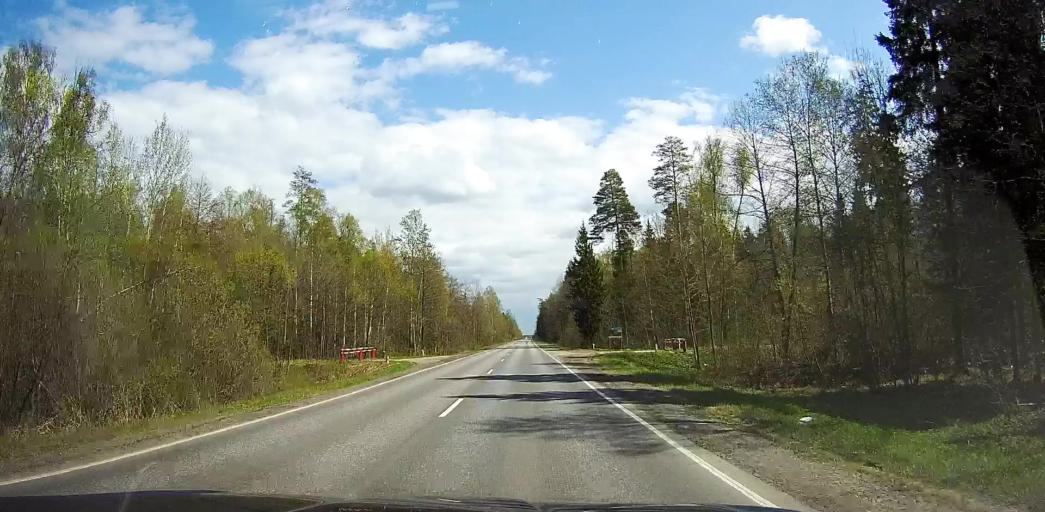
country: RU
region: Moskovskaya
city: Davydovo
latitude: 55.5514
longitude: 38.7710
